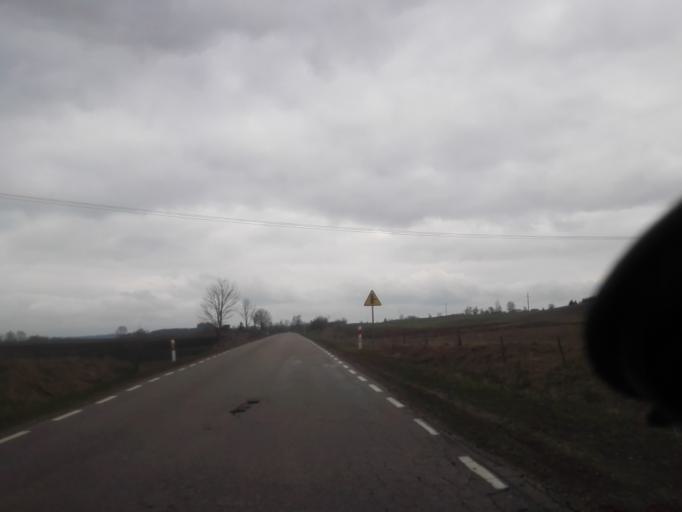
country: PL
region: Podlasie
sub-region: Suwalki
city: Suwalki
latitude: 54.2276
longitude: 22.9122
